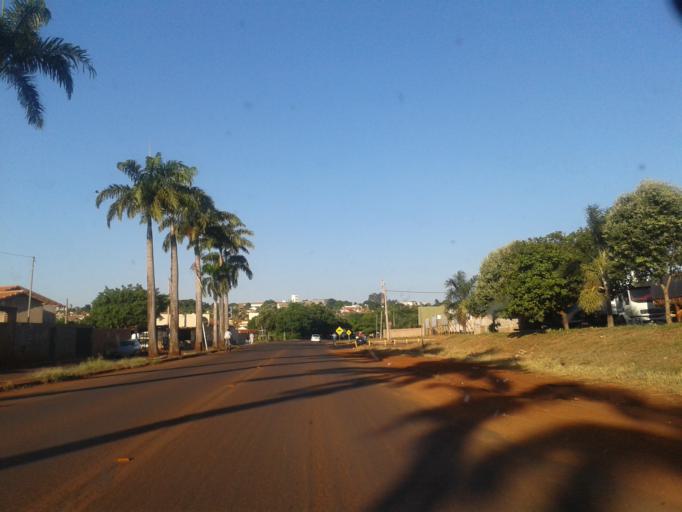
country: BR
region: Minas Gerais
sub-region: Capinopolis
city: Capinopolis
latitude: -18.6866
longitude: -49.5757
